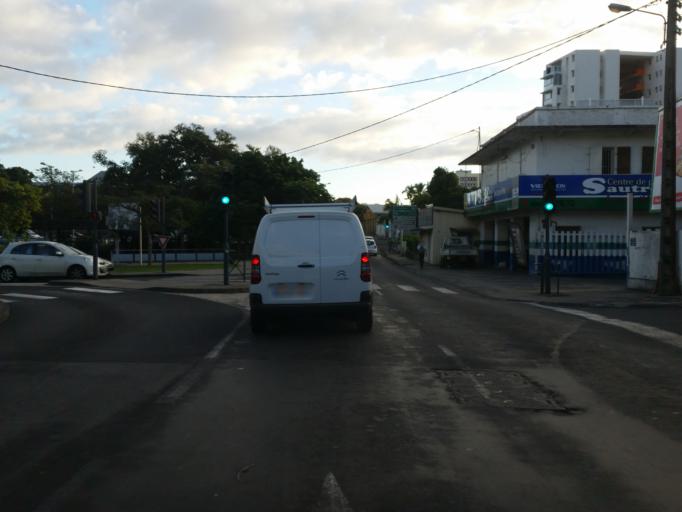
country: RE
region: Reunion
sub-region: Reunion
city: Saint-Denis
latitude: -20.8916
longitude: 55.4549
